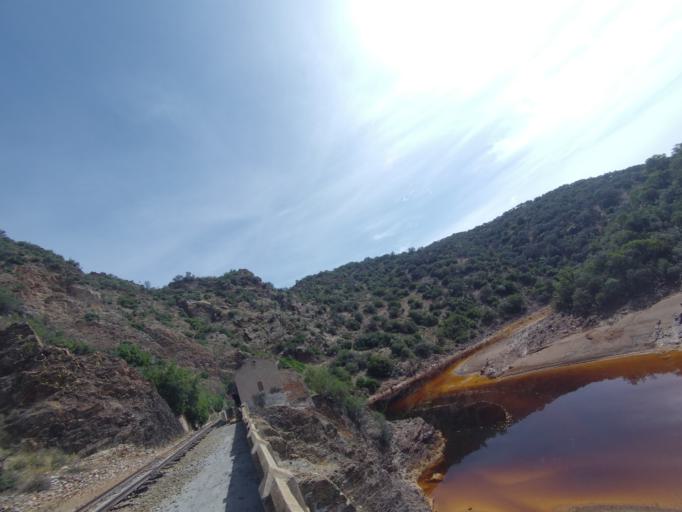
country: ES
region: Andalusia
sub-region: Provincia de Huelva
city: La Palma del Condado
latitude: 37.4792
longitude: -6.5696
